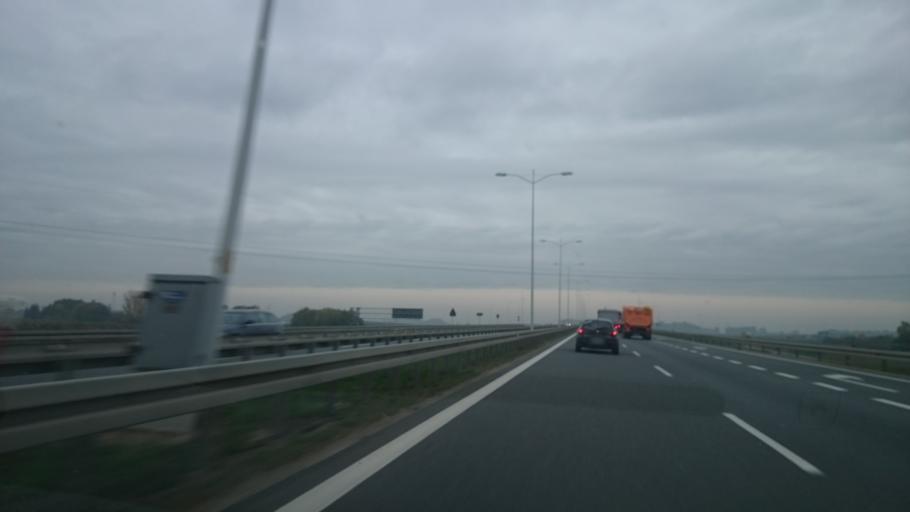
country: PL
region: Lower Silesian Voivodeship
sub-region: Powiat wroclawski
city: Tyniec Maly
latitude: 51.0388
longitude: 16.9366
